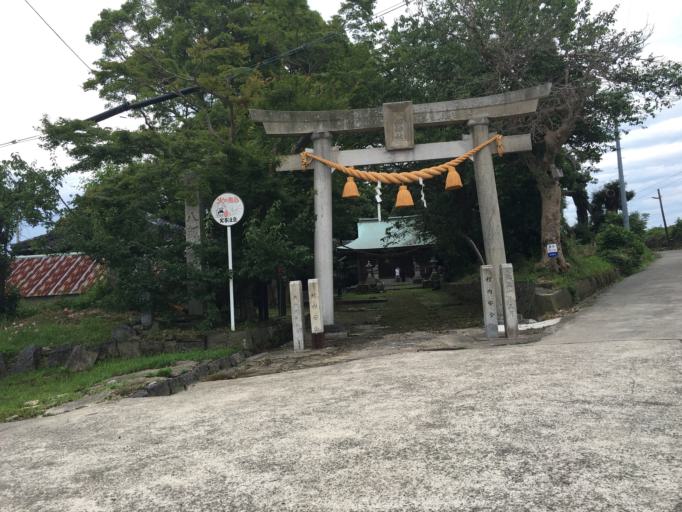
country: JP
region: Aichi
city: Ishiki
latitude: 34.7219
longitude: 137.0485
